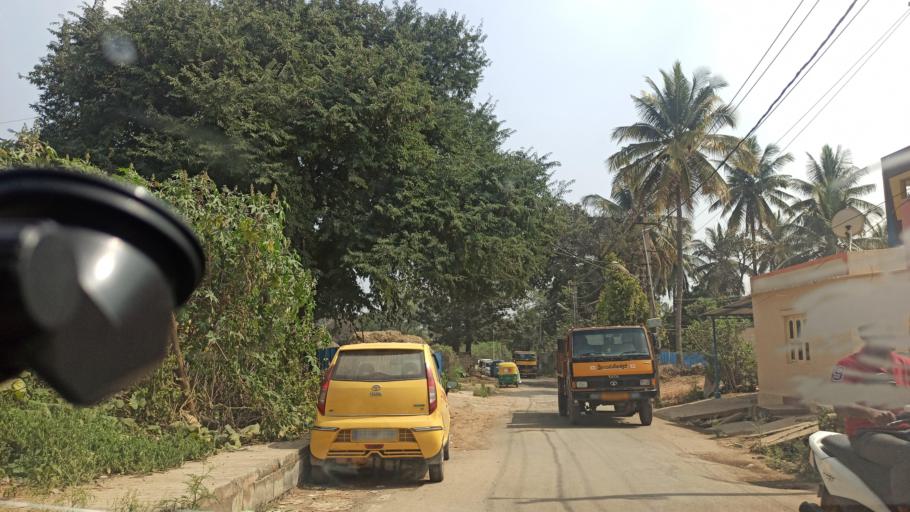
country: IN
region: Karnataka
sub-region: Bangalore Urban
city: Yelahanka
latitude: 13.0793
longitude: 77.6086
